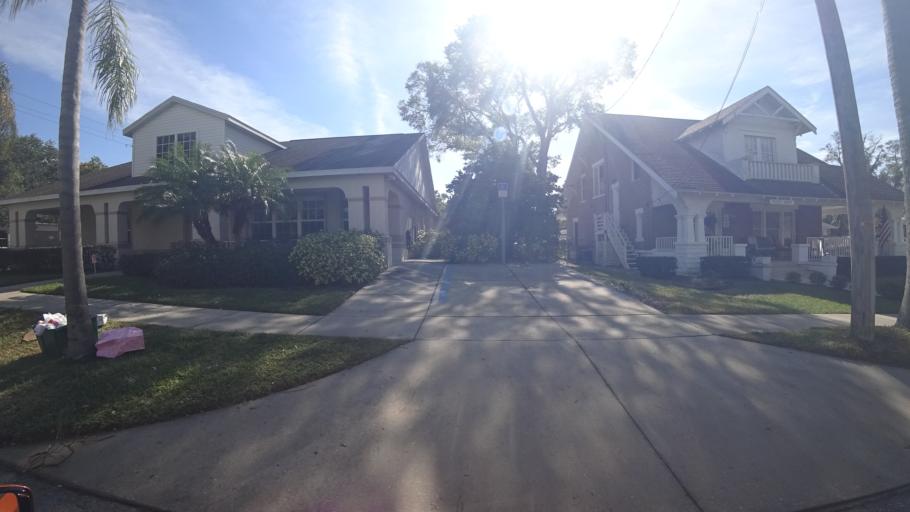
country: US
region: Florida
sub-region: Manatee County
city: Bradenton
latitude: 27.4929
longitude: -82.5762
